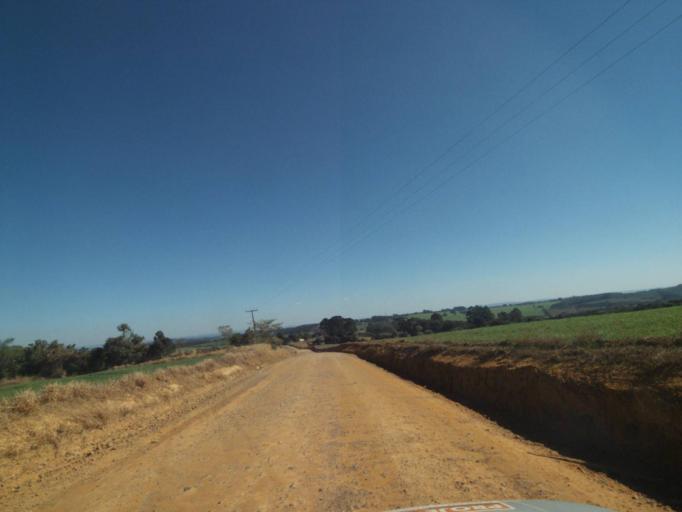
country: BR
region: Parana
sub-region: Tibagi
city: Tibagi
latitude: -24.6193
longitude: -50.6100
